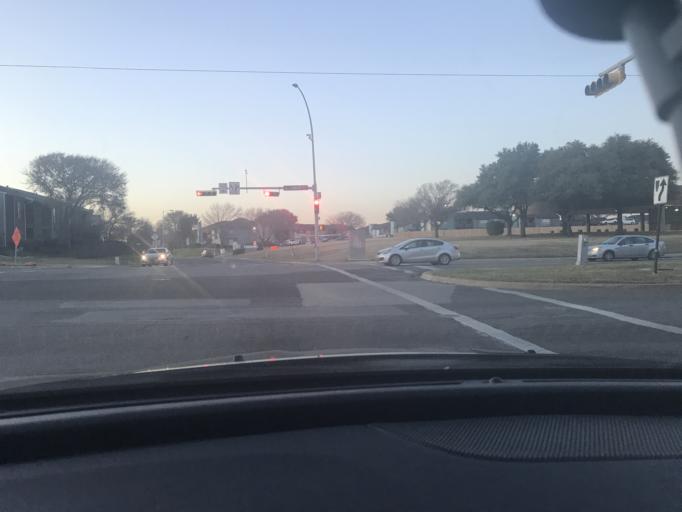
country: US
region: Texas
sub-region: Tarrant County
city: Arlington
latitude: 32.7638
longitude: -97.1023
